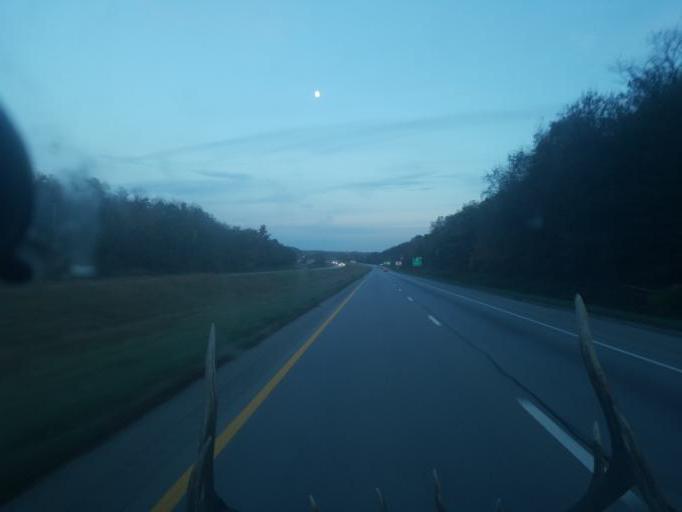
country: US
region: Ohio
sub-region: Guernsey County
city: Cambridge
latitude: 40.0051
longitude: -81.5968
